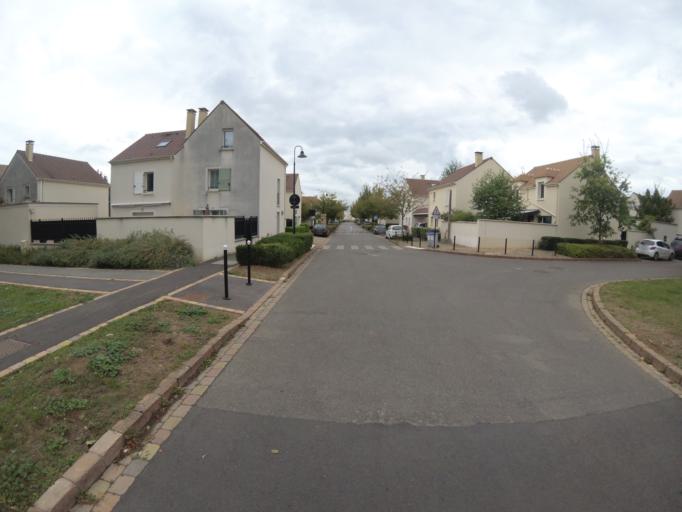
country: FR
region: Ile-de-France
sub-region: Departement de Seine-et-Marne
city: Chessy
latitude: 48.8791
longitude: 2.7687
